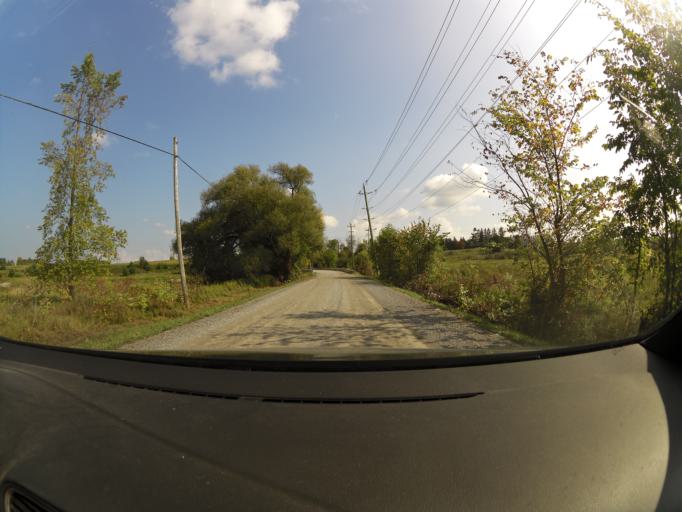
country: CA
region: Ontario
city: Arnprior
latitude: 45.4215
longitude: -76.2518
